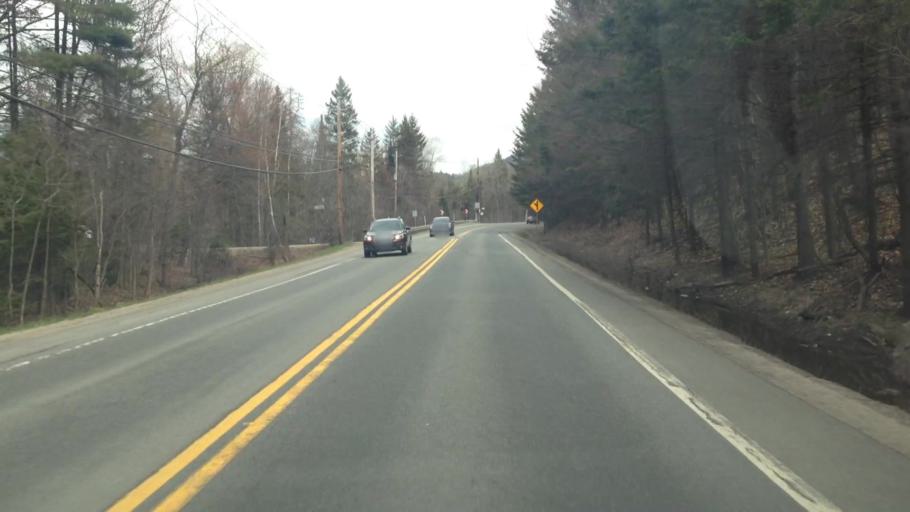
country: CA
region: Quebec
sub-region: Laurentides
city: Sainte-Adele
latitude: 45.9738
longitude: -74.1172
